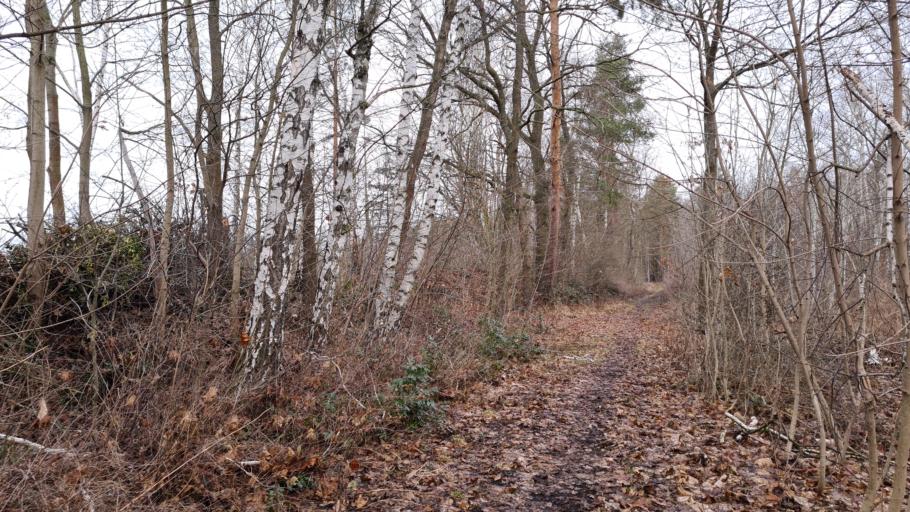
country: DE
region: Brandenburg
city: Sallgast
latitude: 51.5612
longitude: 13.8741
